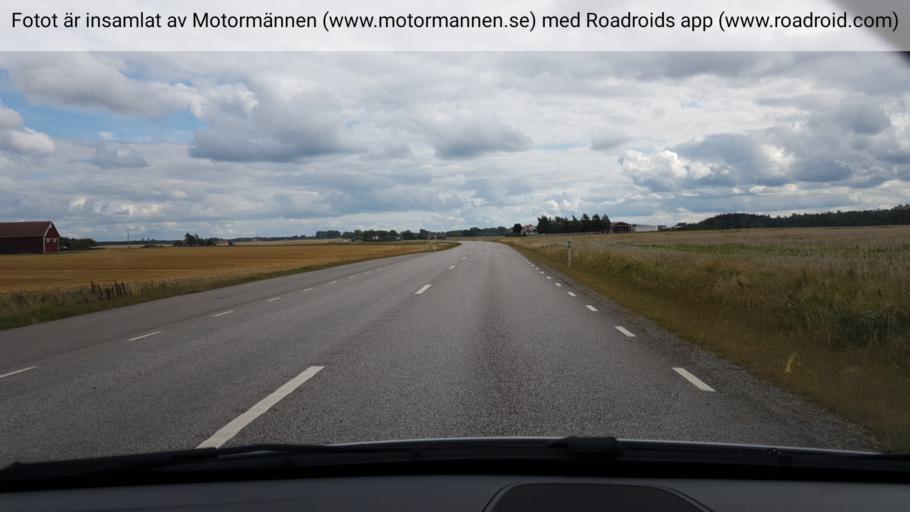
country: SE
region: Vaestra Goetaland
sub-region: Vara Kommun
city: Kvanum
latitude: 58.2330
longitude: 13.1342
